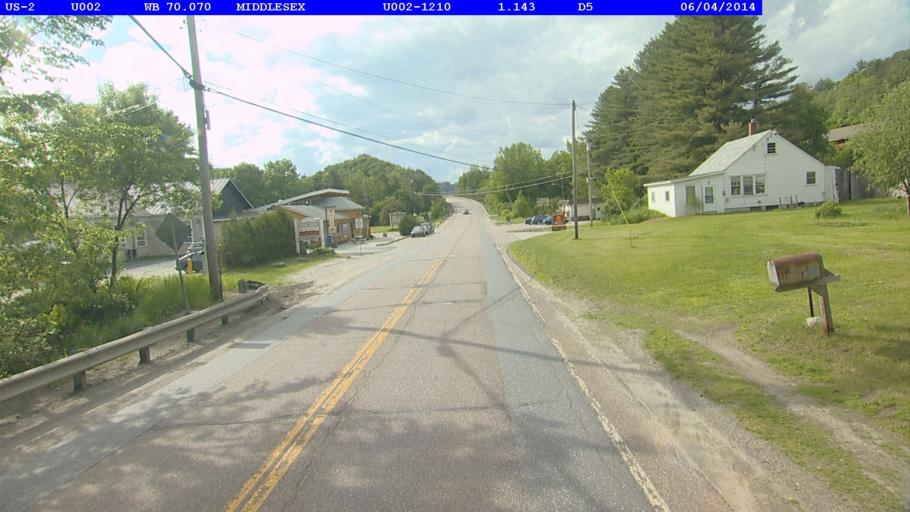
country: US
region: Vermont
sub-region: Washington County
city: Waterbury
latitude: 44.2940
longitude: -72.6820
